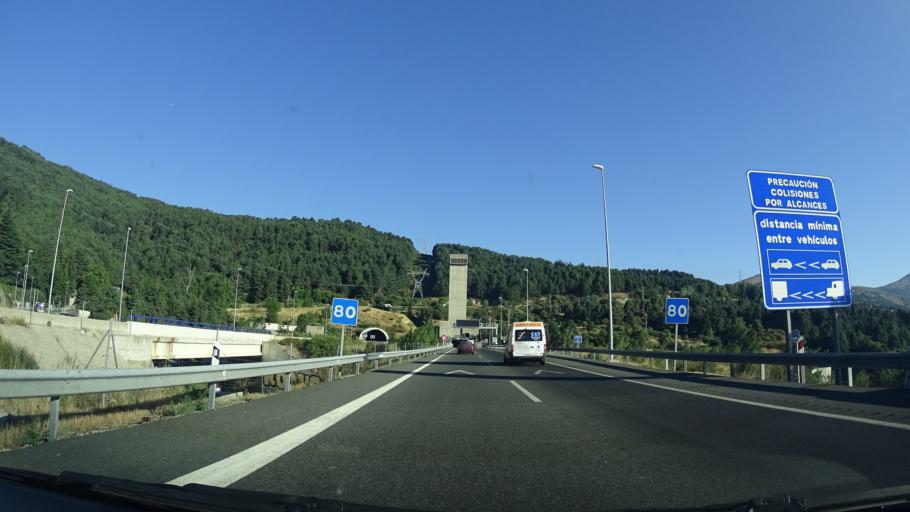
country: ES
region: Madrid
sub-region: Provincia de Madrid
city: Guadarrama
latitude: 40.6977
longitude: -4.1273
